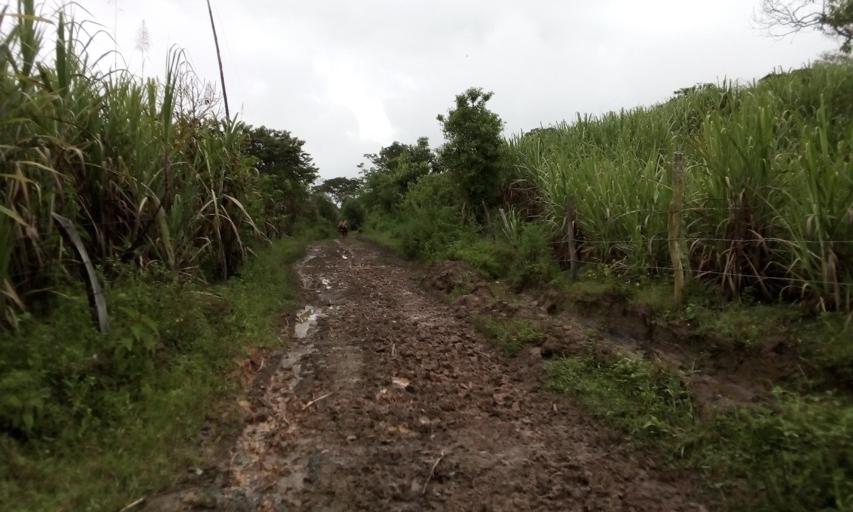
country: CO
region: Boyaca
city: Santana
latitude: 5.9981
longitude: -73.4986
